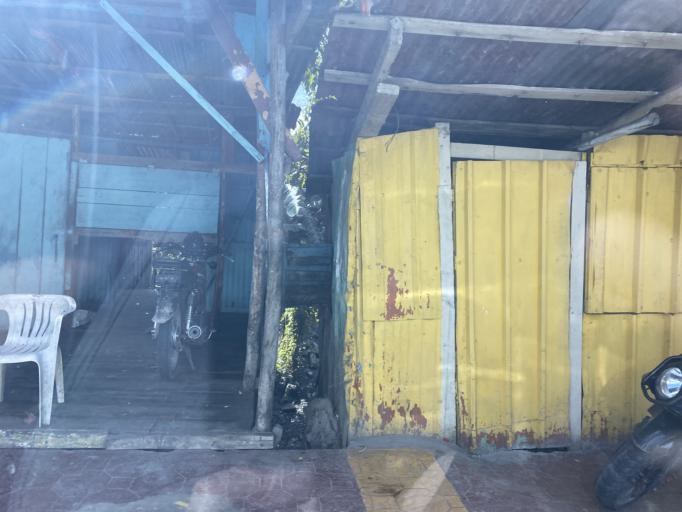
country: DO
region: Espaillat
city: Jamao al Norte
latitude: 19.6669
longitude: -70.3673
